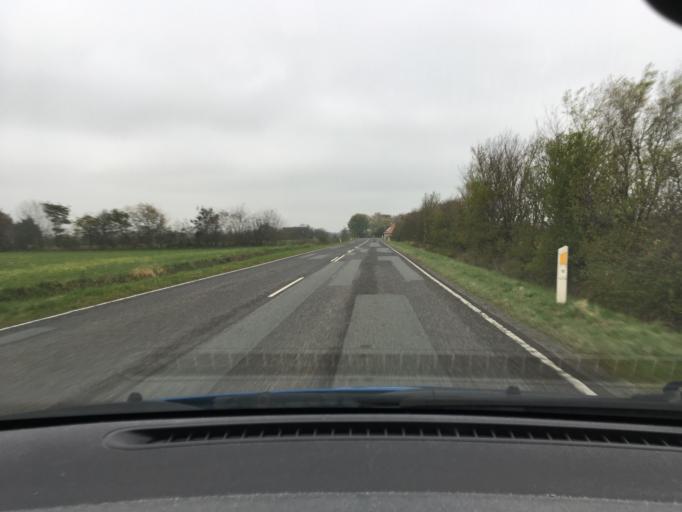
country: DK
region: South Denmark
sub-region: Aabenraa Kommune
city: Rodekro
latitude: 55.0709
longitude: 9.1851
